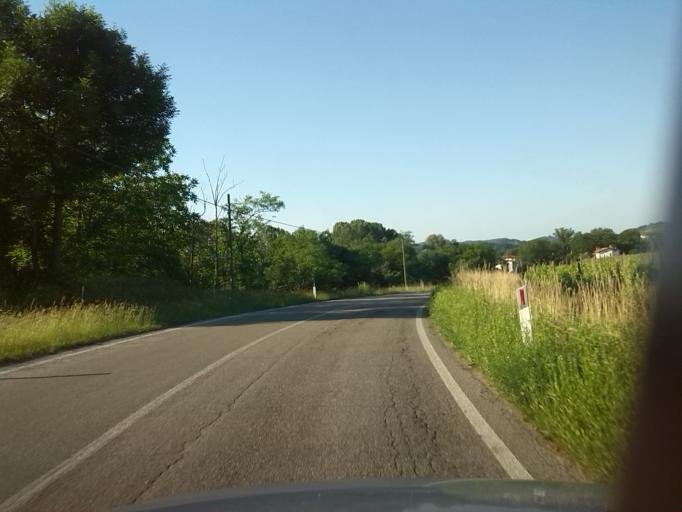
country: IT
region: Friuli Venezia Giulia
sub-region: Provincia di Gorizia
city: Dolegna del Collio
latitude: 46.0370
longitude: 13.4779
